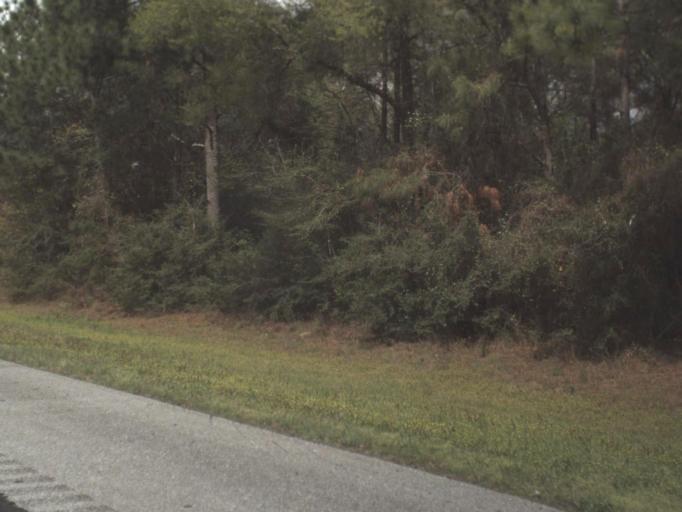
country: US
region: Florida
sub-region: Okaloosa County
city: Crestview
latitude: 30.7104
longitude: -86.7135
